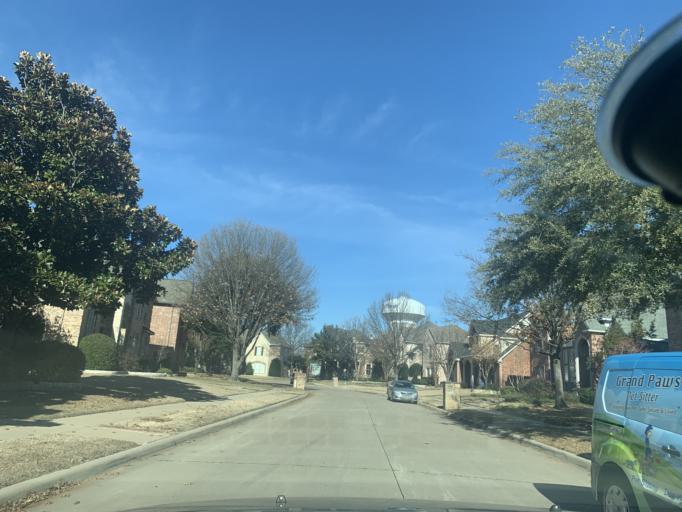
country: US
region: Texas
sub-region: Denton County
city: The Colony
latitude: 33.0542
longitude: -96.8217
